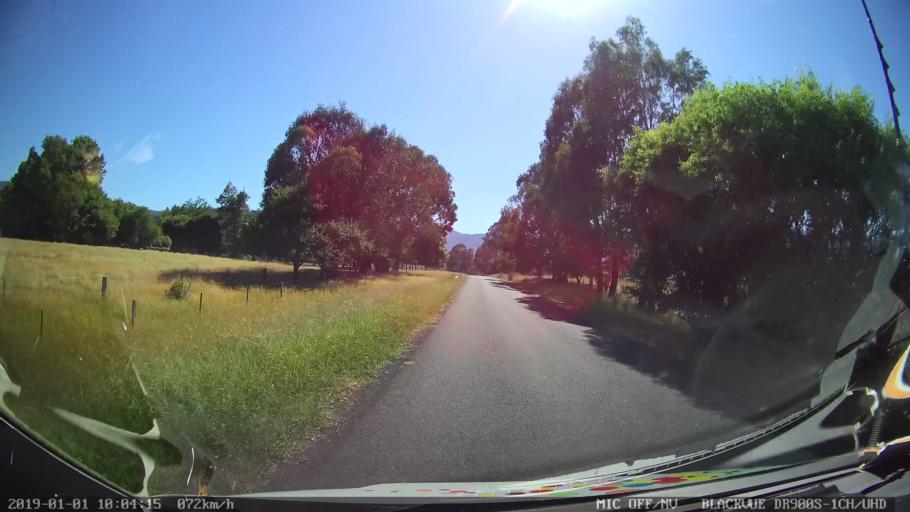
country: AU
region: New South Wales
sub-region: Snowy River
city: Jindabyne
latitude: -36.1765
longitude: 148.1201
